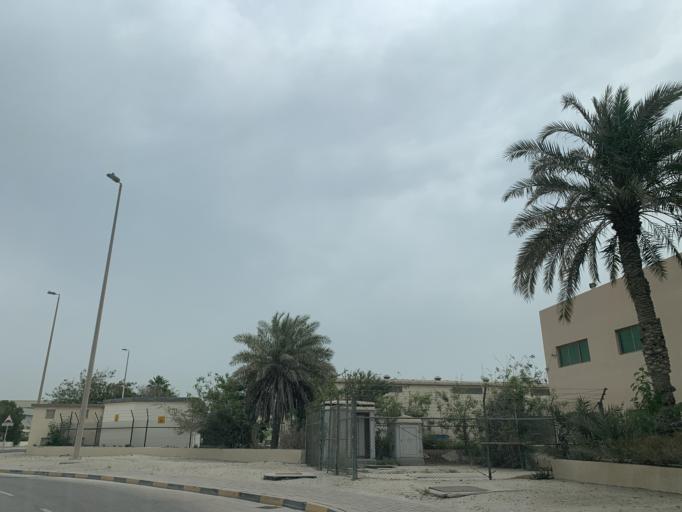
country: BH
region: Muharraq
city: Al Hadd
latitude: 26.2159
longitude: 50.6603
